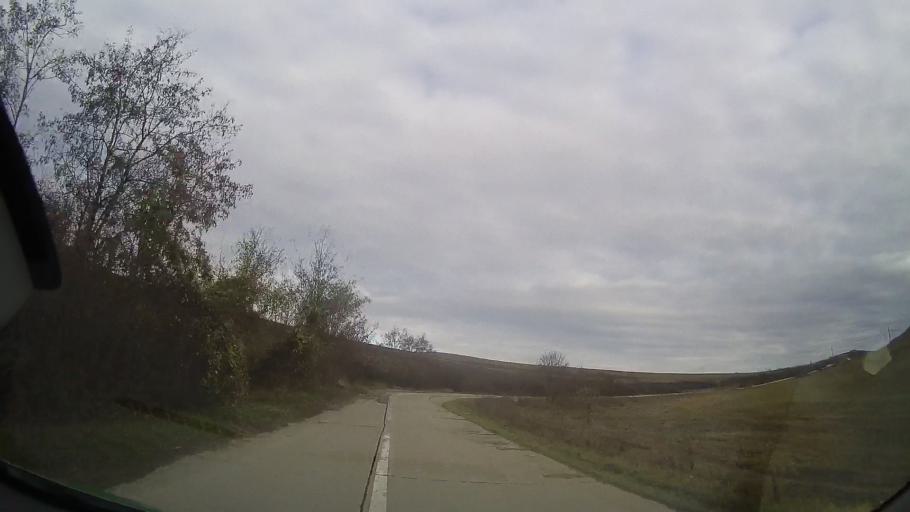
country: RO
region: Bistrita-Nasaud
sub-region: Comuna Micestii de Campie
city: Micestii de Campie
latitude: 46.8486
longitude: 24.3039
